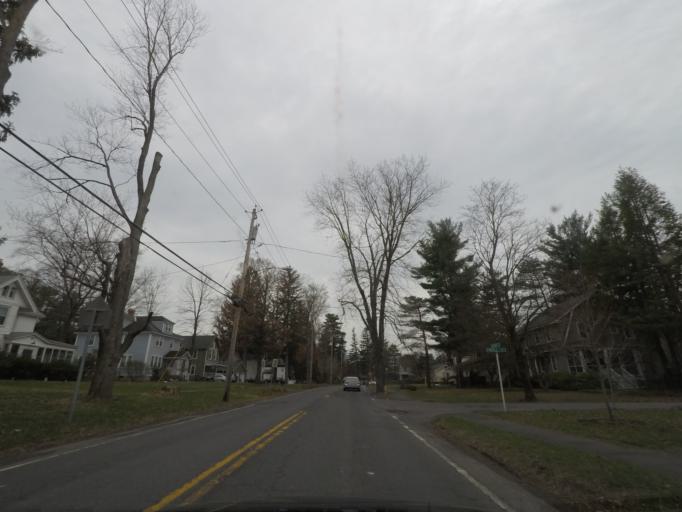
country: US
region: New York
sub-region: Albany County
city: Delmar
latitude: 42.6233
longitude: -73.8206
